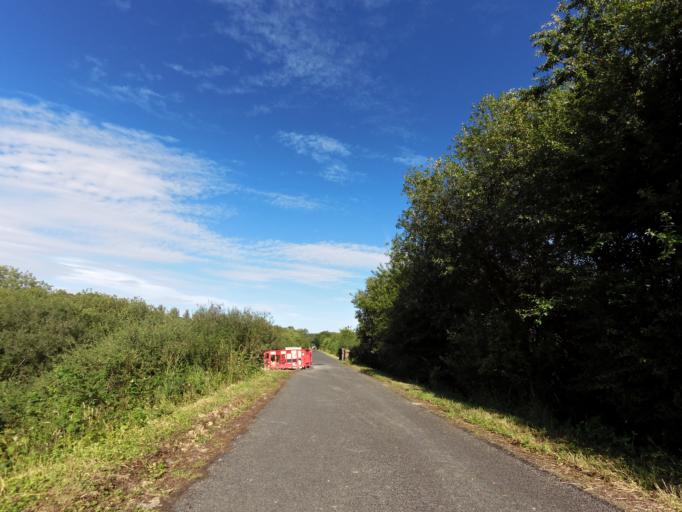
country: IE
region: Munster
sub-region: Waterford
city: Portlaw
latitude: 52.2260
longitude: -7.3303
